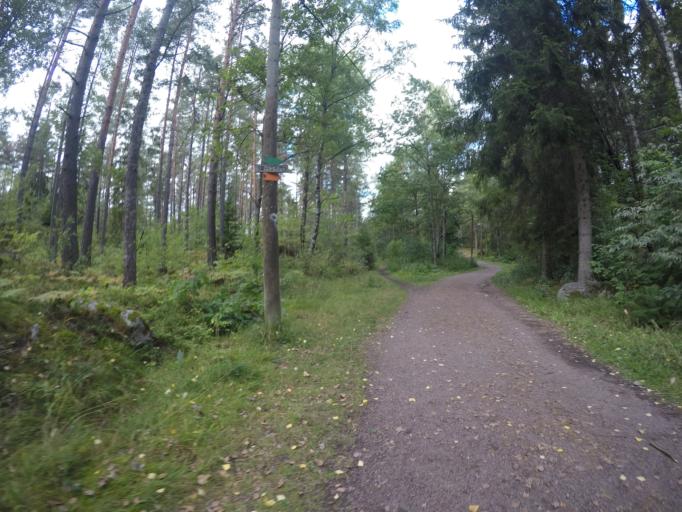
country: SE
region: Vaestmanland
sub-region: Vasteras
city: Vasteras
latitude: 59.6387
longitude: 16.5209
